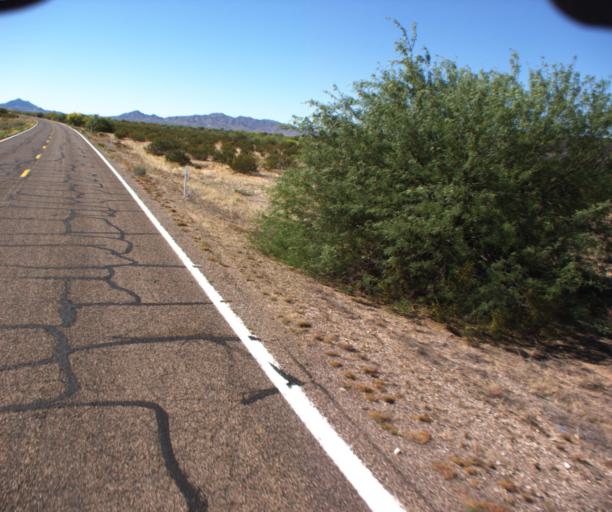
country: US
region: Arizona
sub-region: Pima County
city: Ajo
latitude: 32.4910
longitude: -112.8816
